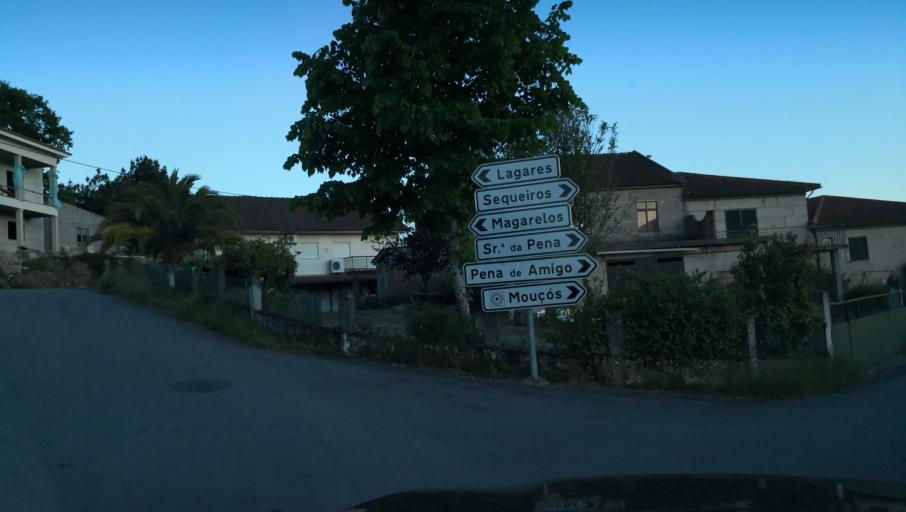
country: PT
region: Vila Real
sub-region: Vila Real
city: Vila Real
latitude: 41.3208
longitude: -7.6769
